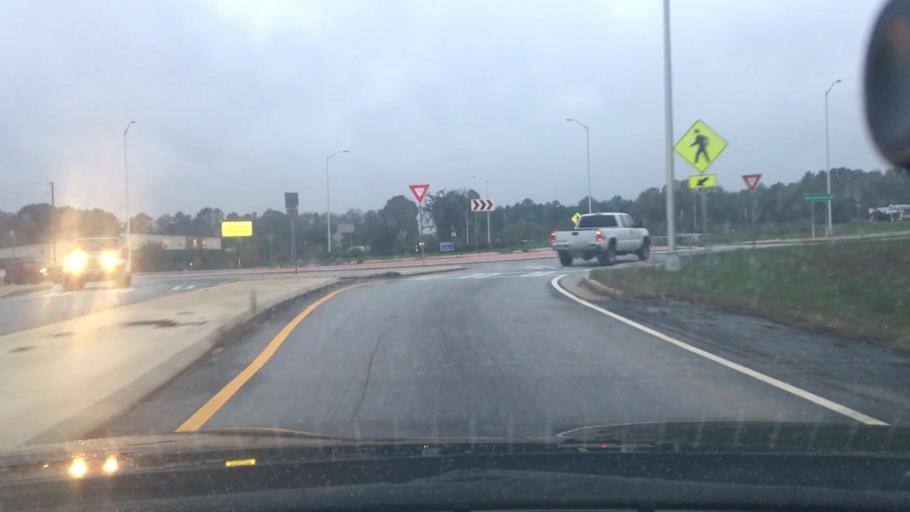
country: US
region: Georgia
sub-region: Coweta County
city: Senoia
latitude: 33.2545
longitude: -84.4887
